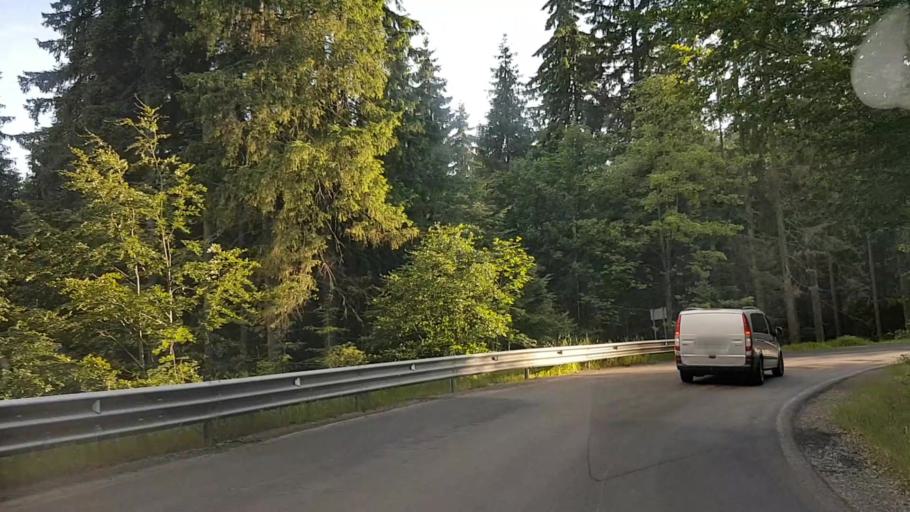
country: RO
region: Harghita
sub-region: Comuna Varsag
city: Varsag
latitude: 46.6644
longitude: 25.3053
